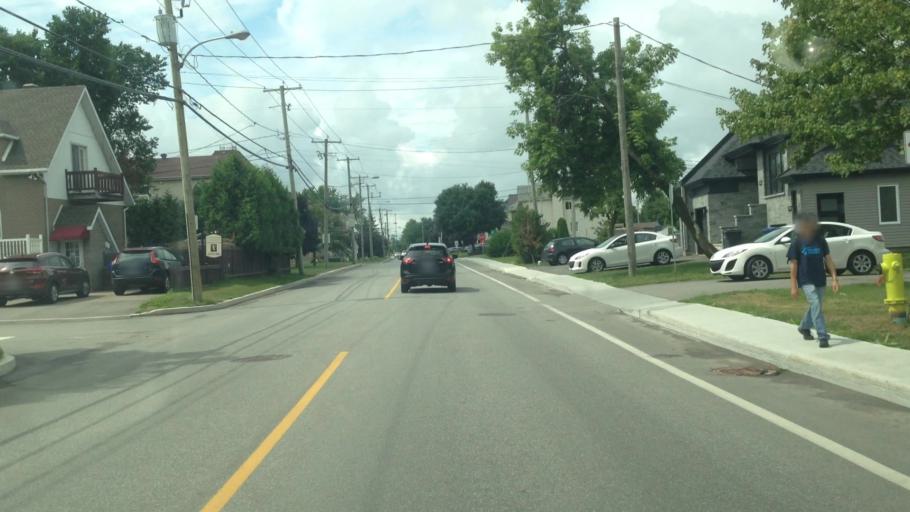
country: CA
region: Quebec
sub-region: Laurentides
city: Blainville
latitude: 45.7001
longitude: -73.9333
